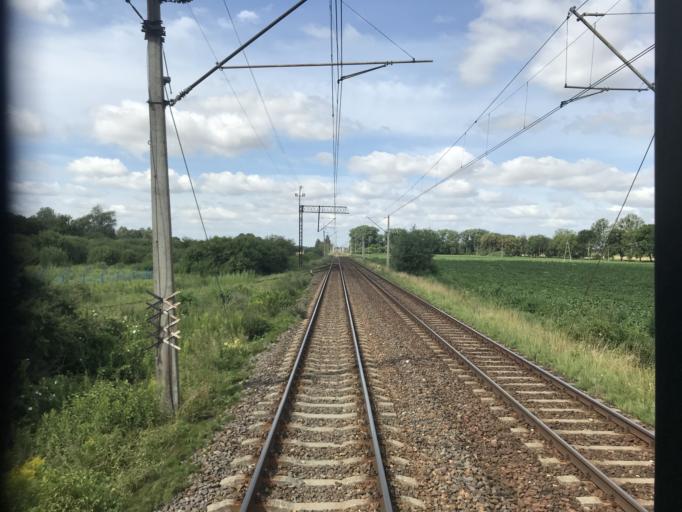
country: PL
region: Pomeranian Voivodeship
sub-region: Powiat malborski
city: Stare Pole
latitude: 54.0388
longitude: 19.1284
